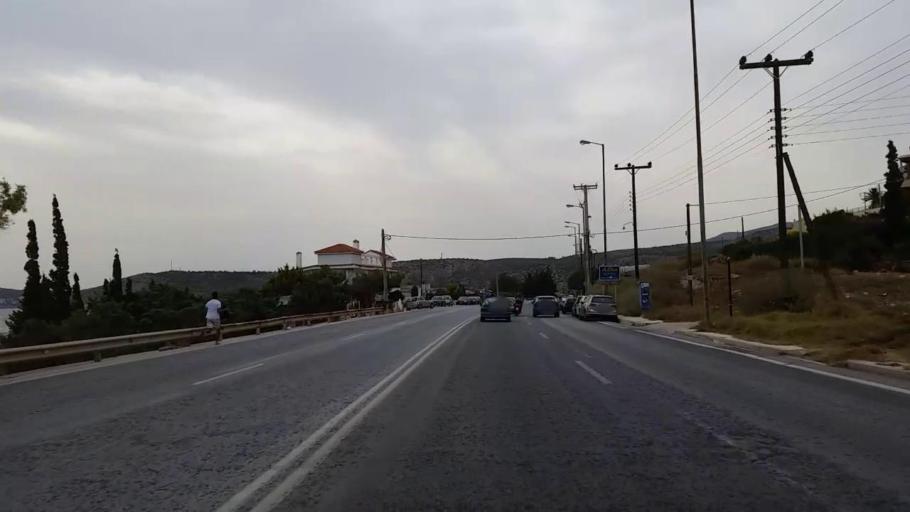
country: GR
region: Attica
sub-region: Nomarchia Anatolikis Attikis
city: Agios Dimitrios Kropias
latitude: 37.8079
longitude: 23.8490
